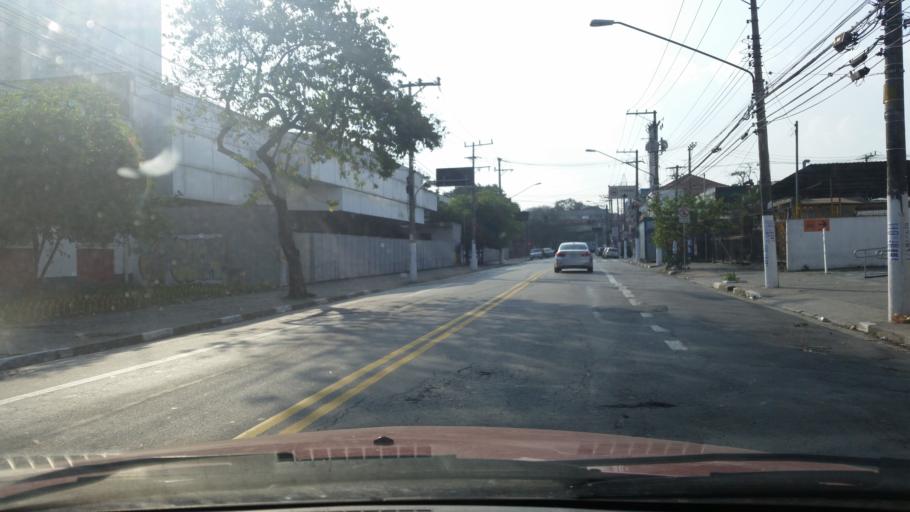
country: BR
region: Sao Paulo
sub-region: Osasco
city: Osasco
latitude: -23.5253
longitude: -46.7361
